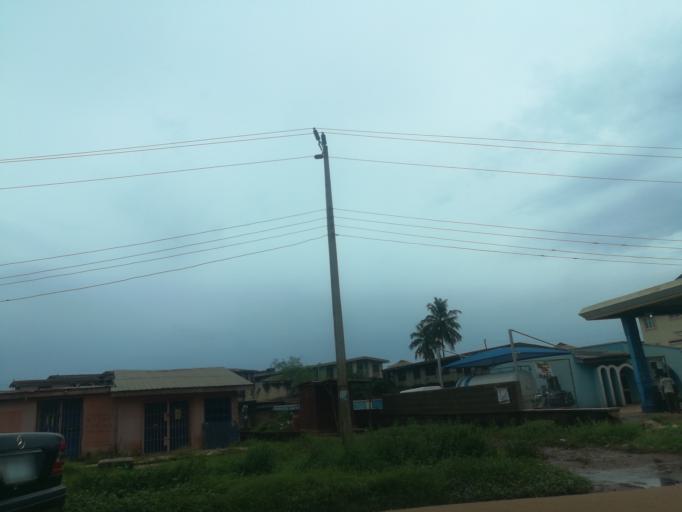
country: NG
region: Oyo
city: Ibadan
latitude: 7.3917
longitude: 3.9652
